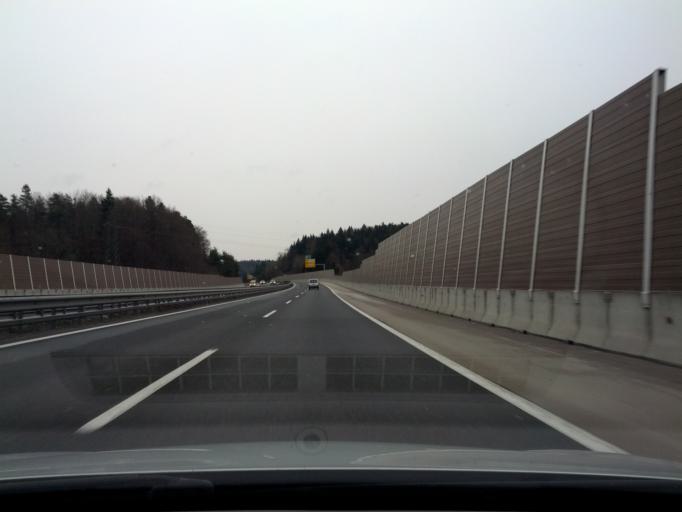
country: SI
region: Grosuplje
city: Grosuplje
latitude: 45.9696
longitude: 14.6440
